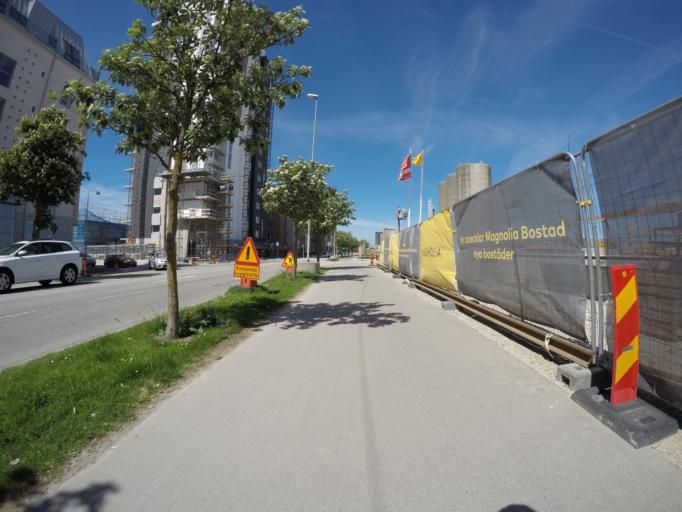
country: SE
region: Skane
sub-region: Malmo
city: Bunkeflostrand
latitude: 55.5867
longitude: 12.9281
